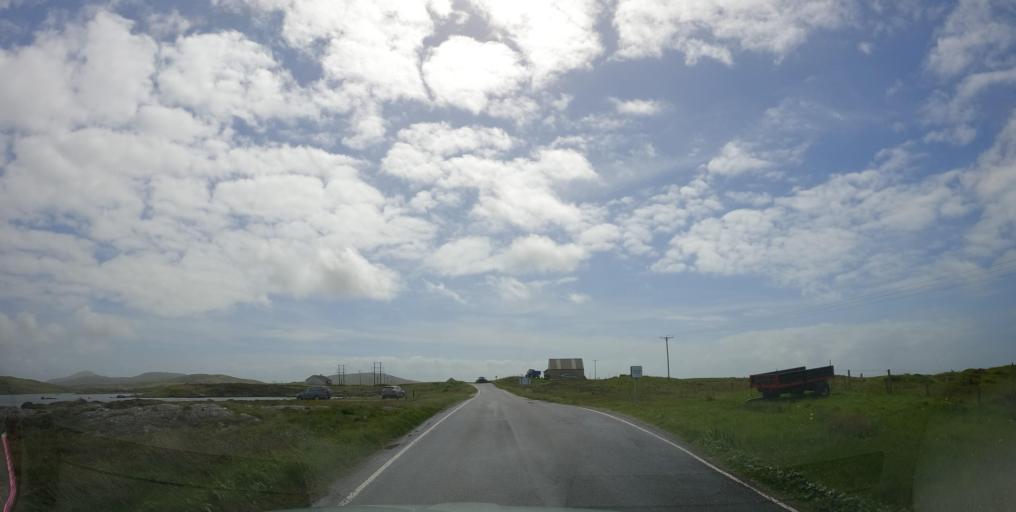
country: GB
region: Scotland
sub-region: Eilean Siar
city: Isle of South Uist
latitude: 57.2197
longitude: -7.3971
